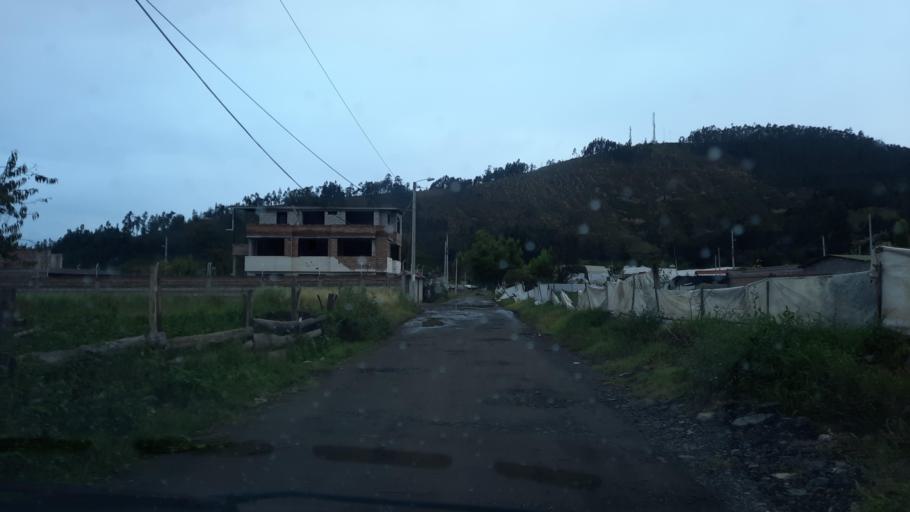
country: EC
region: Chimborazo
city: Riobamba
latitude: -1.6872
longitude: -78.6651
